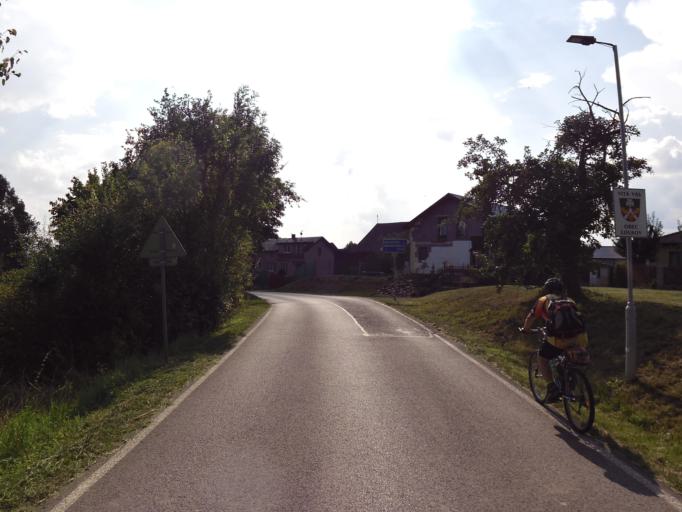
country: CZ
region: Central Bohemia
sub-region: Okres Mlada Boleslav
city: Zd'ar
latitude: 50.5644
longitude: 15.0363
